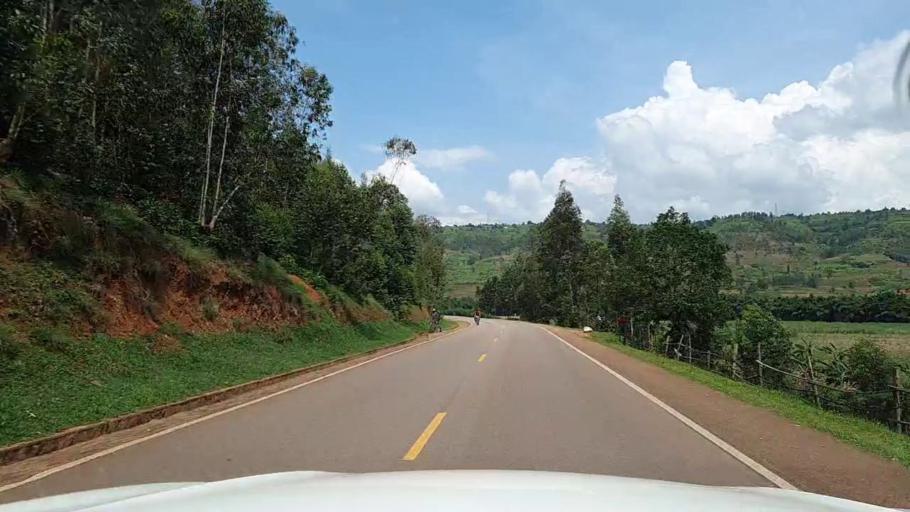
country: RW
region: Kigali
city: Kigali
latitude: -1.8482
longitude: 30.0960
